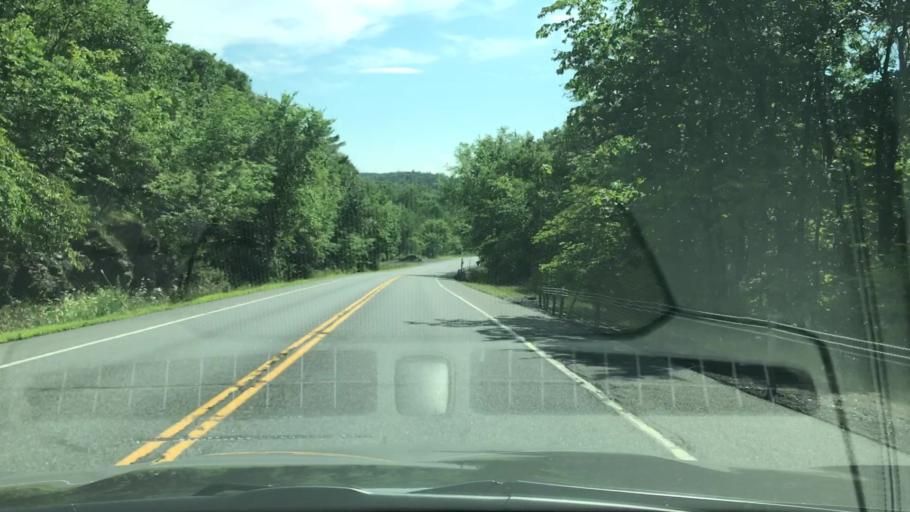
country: US
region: Vermont
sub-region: Rutland County
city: Fair Haven
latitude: 43.5642
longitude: -73.3307
